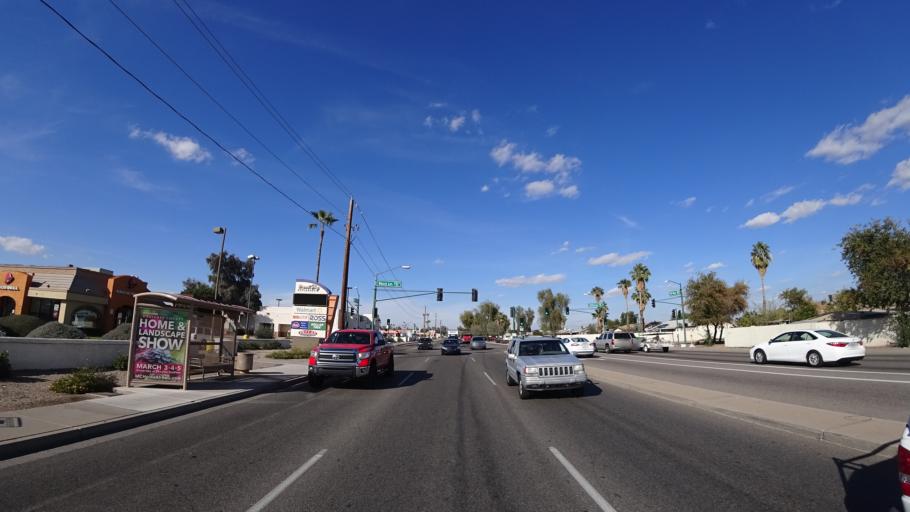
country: US
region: Arizona
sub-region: Maricopa County
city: Tolleson
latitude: 33.4690
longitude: -112.2208
